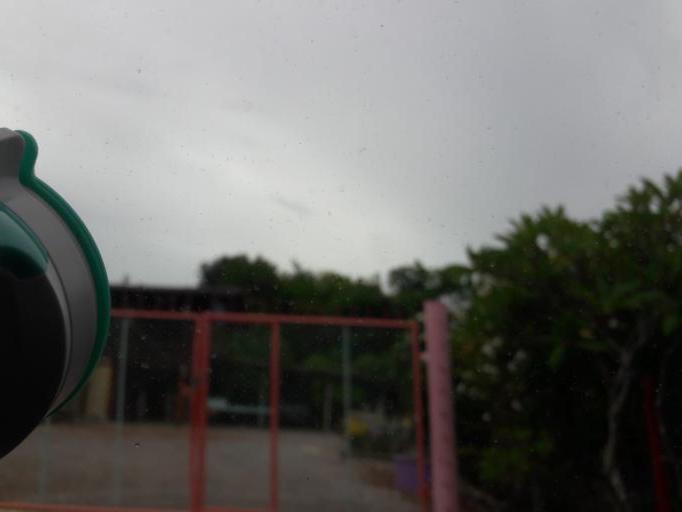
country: TH
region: Ratchaburi
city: Damnoen Saduak
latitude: 13.5395
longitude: 100.0024
